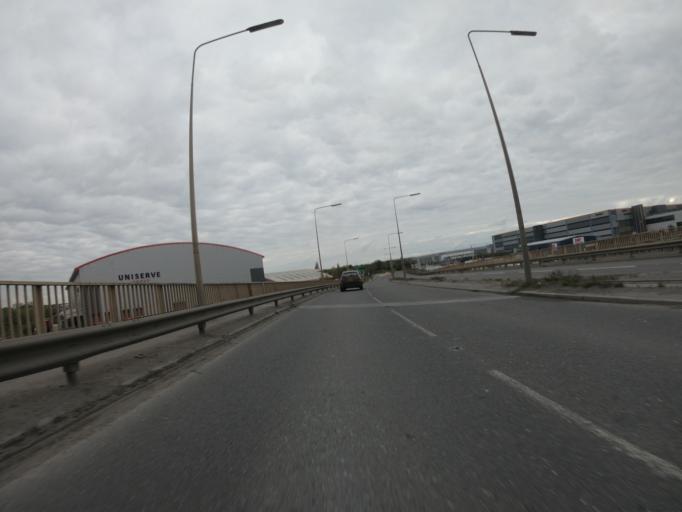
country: GB
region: England
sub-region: Borough of Thurrock
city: Tilbury
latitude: 51.4662
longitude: 0.3474
